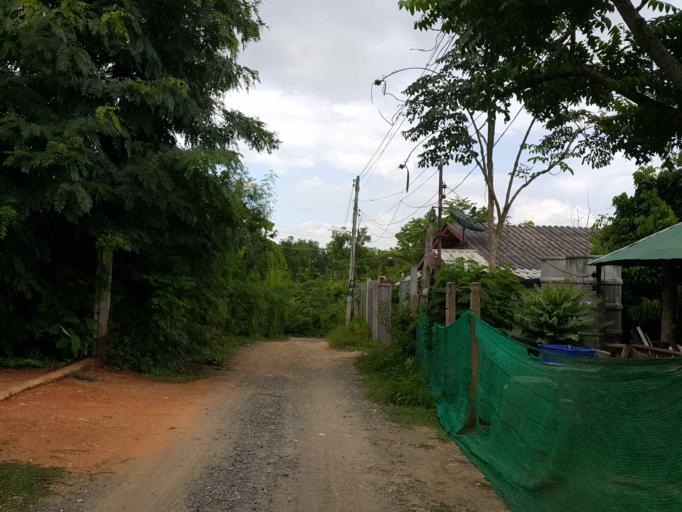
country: TH
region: Chiang Mai
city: San Sai
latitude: 18.9345
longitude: 98.9180
